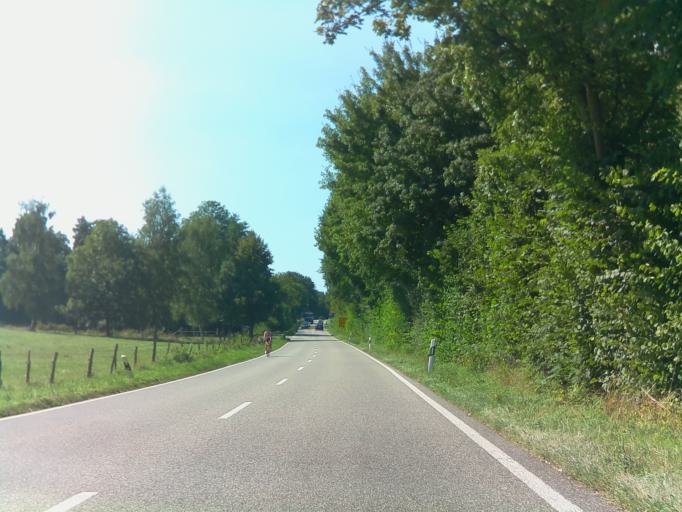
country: DE
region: Baden-Wuerttemberg
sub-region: Karlsruhe Region
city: Oberderdingen
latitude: 49.0925
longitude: 8.7622
